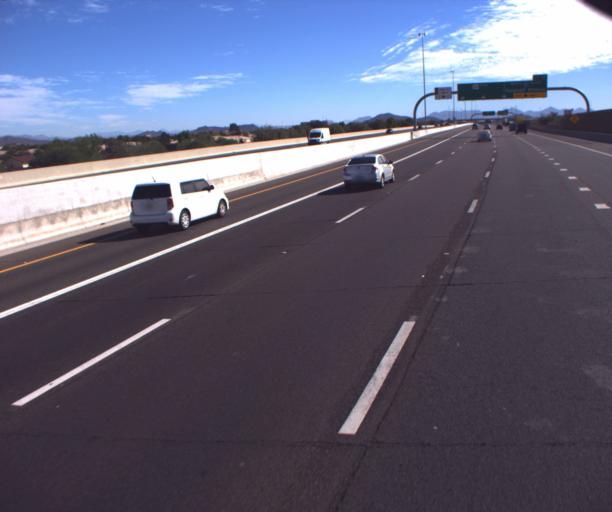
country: US
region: Arizona
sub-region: Maricopa County
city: Peoria
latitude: 33.6686
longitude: -112.1317
